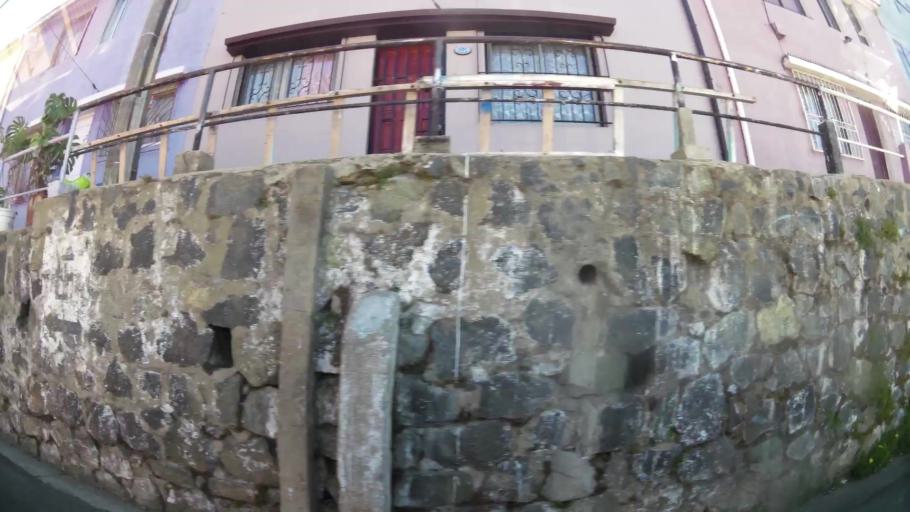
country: CL
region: Valparaiso
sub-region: Provincia de Valparaiso
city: Valparaiso
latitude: -33.0253
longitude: -71.6336
